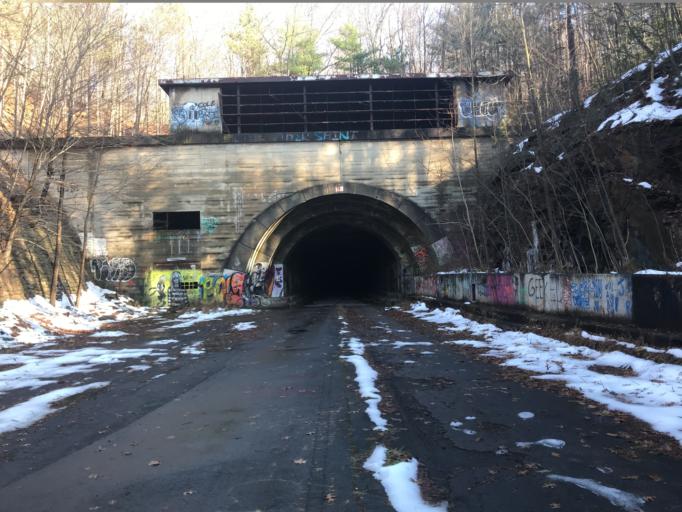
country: US
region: Pennsylvania
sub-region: Fulton County
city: McConnellsburg
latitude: 40.0497
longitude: -78.1415
